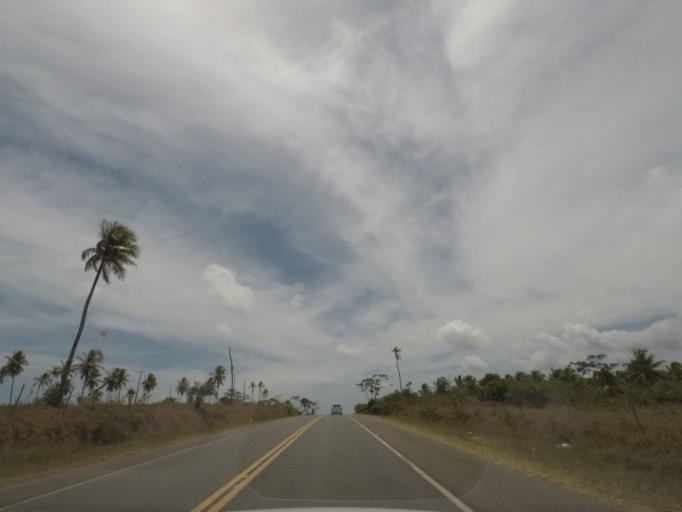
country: BR
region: Bahia
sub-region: Conde
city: Conde
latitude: -11.8375
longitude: -37.6353
